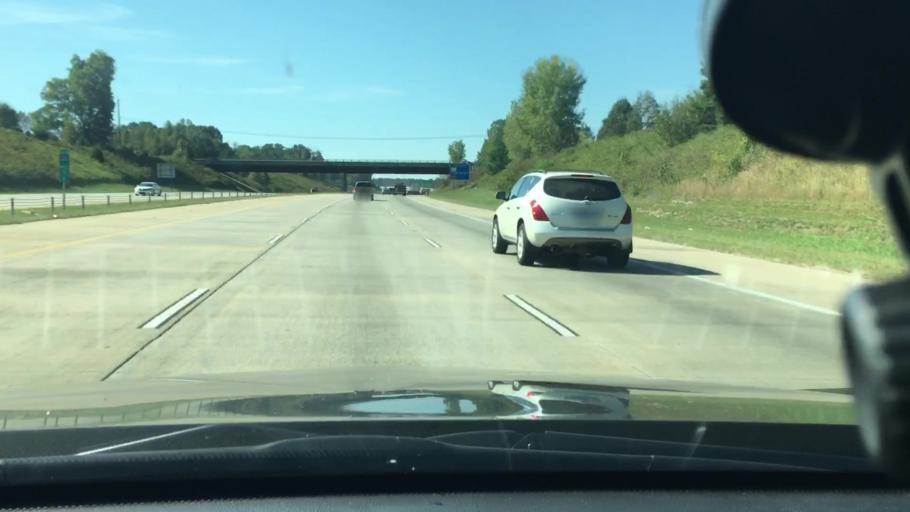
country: US
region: North Carolina
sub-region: Gaston County
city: Mount Holly
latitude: 35.2987
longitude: -80.9577
